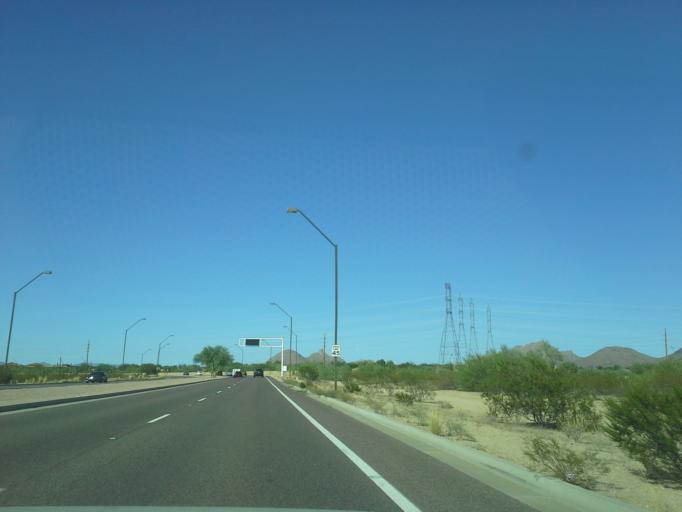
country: US
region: Arizona
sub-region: Maricopa County
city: Paradise Valley
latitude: 33.6635
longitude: -111.9054
